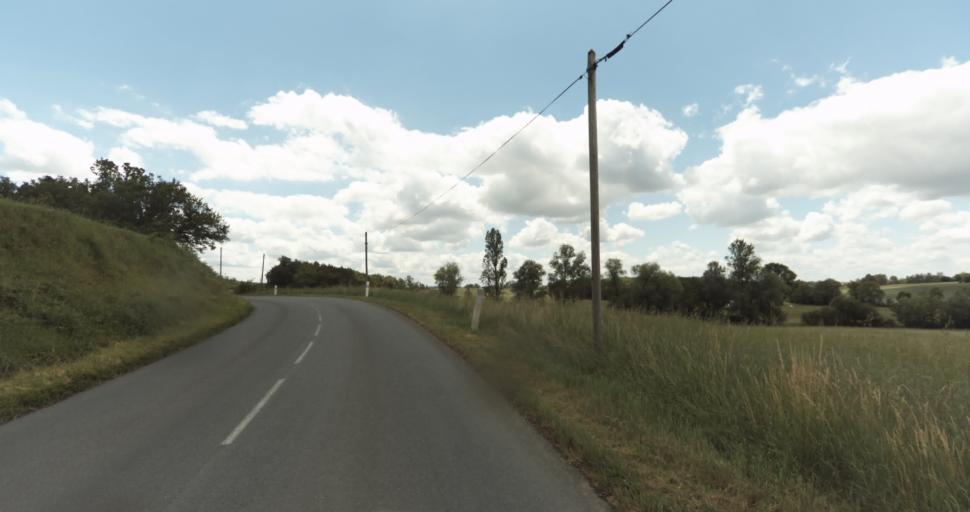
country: FR
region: Aquitaine
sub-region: Departement du Lot-et-Garonne
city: Villereal
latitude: 44.6853
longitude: 0.7563
